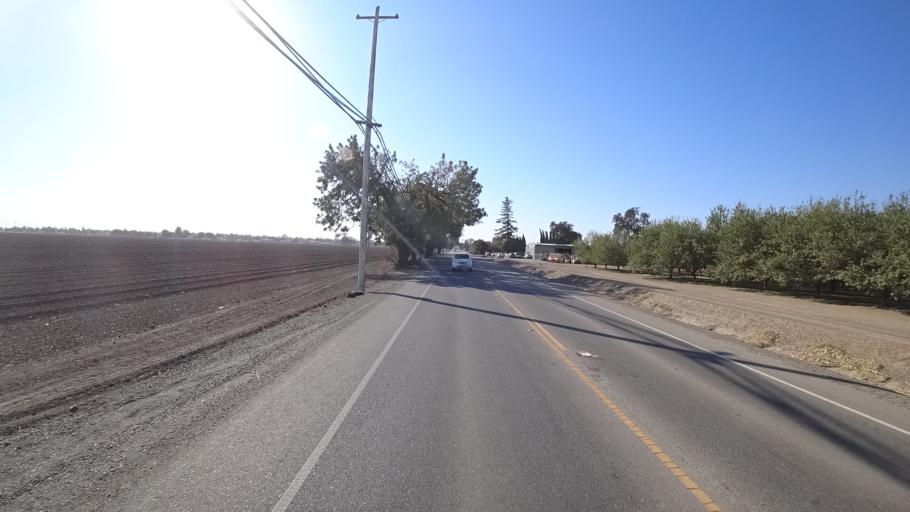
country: US
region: California
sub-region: Yolo County
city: Woodland
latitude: 38.6989
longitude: -121.7839
